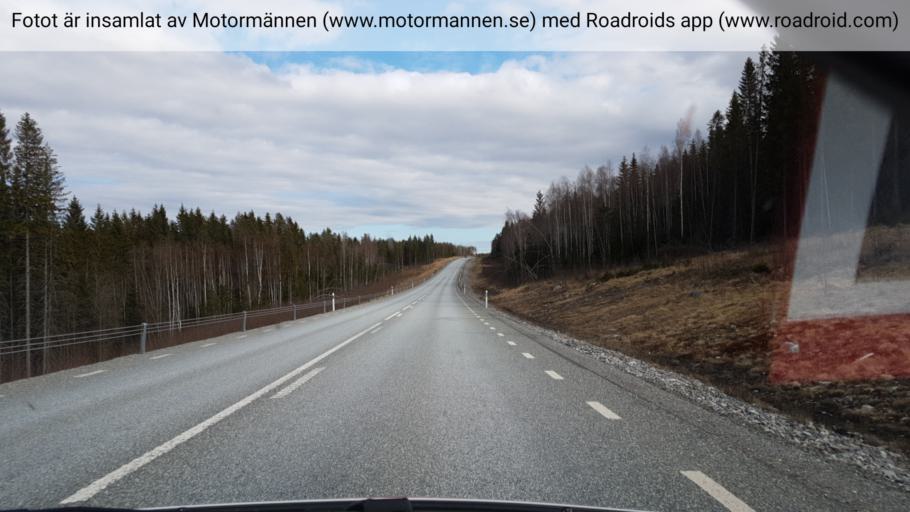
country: SE
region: Vaesternorrland
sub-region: Kramfors Kommun
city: Bollstabruk
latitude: 63.0632
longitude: 17.5943
